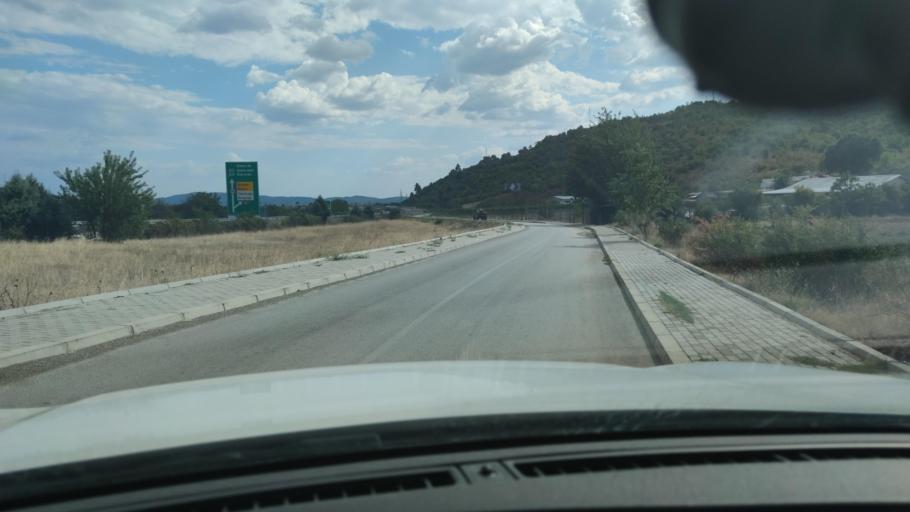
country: MK
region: Gevgelija
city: Gevgelija
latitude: 41.1627
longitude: 22.5067
